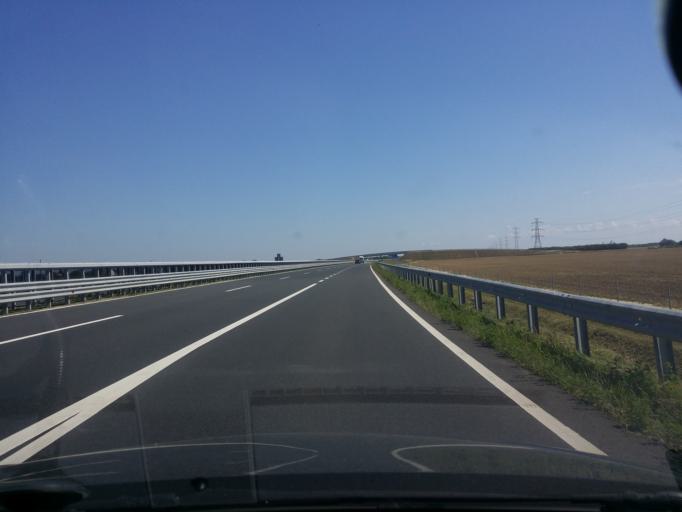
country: HU
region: Vas
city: Sarvar
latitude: 47.3589
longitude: 16.9075
